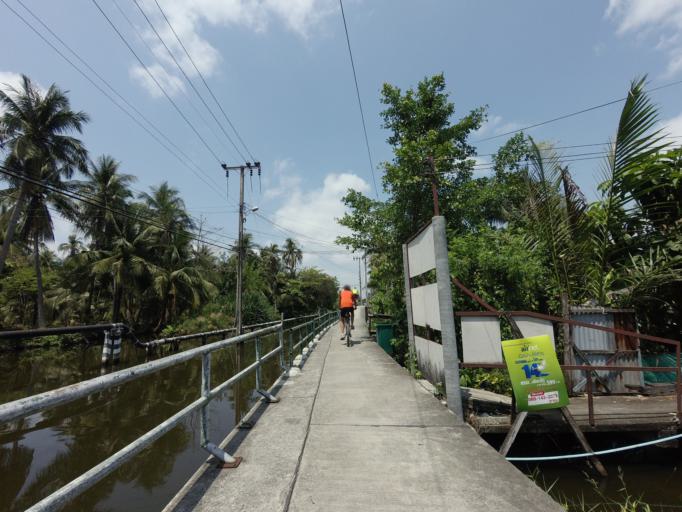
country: TH
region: Bangkok
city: Thung Khru
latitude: 13.6395
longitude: 100.4735
